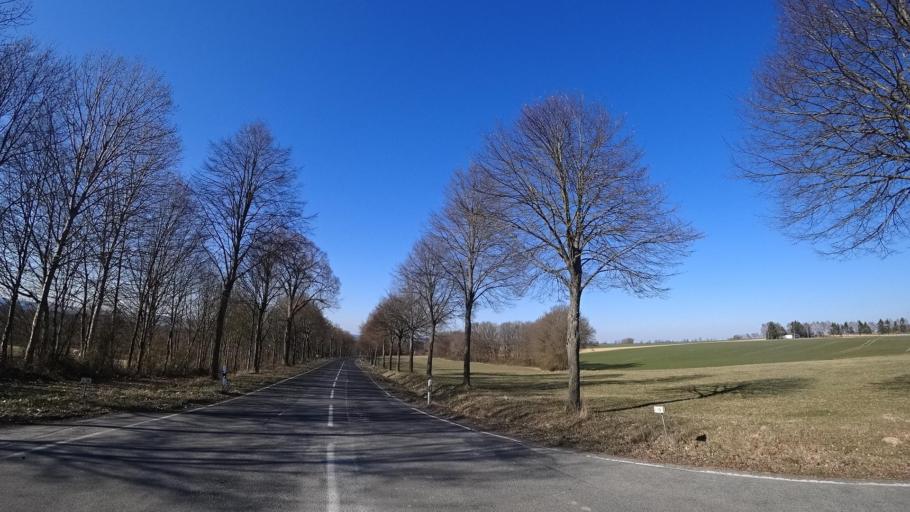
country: DE
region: Rheinland-Pfalz
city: Holzbach
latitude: 49.9483
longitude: 7.5381
